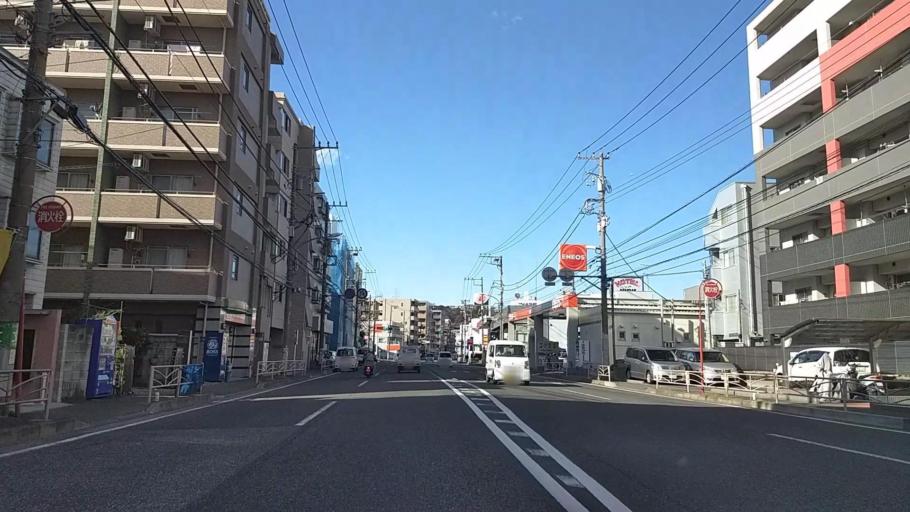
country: JP
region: Kanagawa
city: Yokohama
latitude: 35.3896
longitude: 139.6159
